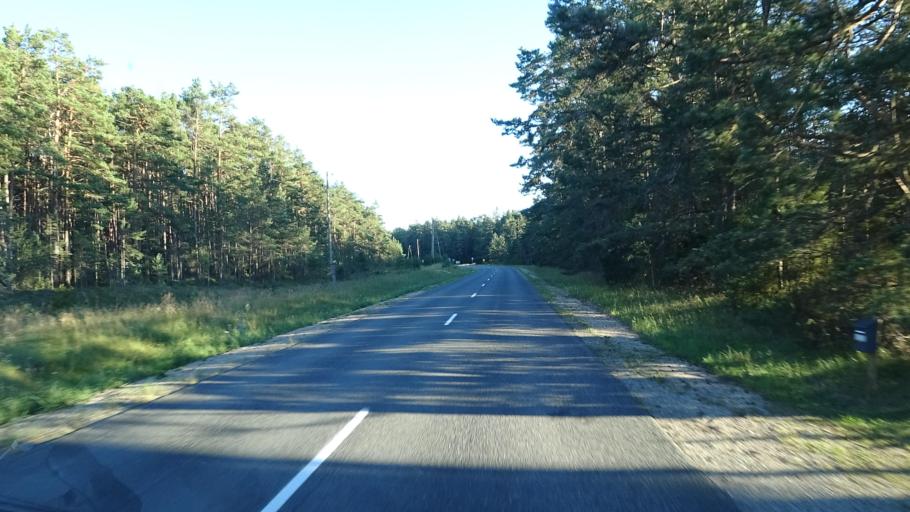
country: LV
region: Dundaga
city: Dundaga
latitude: 57.6803
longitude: 22.5691
